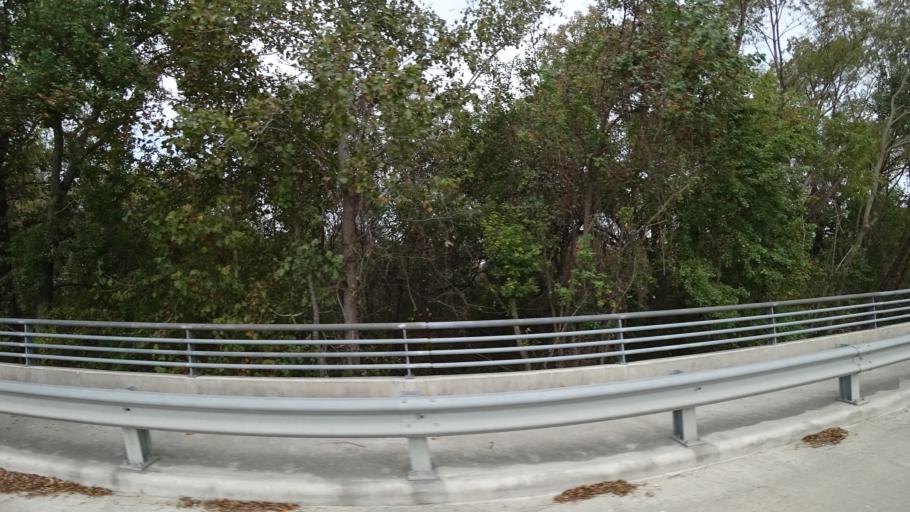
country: US
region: Texas
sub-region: Travis County
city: Windemere
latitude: 30.4614
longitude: -97.6480
